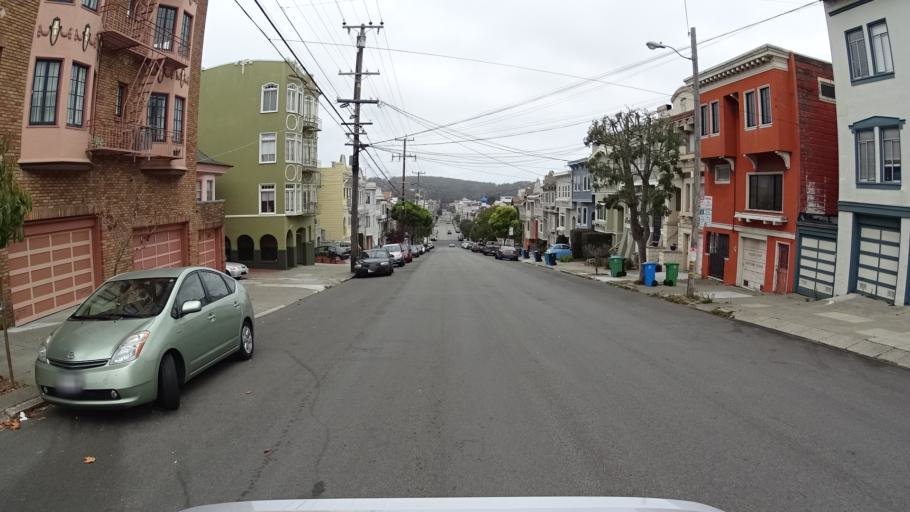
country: US
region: California
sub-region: San Francisco County
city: San Francisco
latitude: 37.7772
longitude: -122.4704
